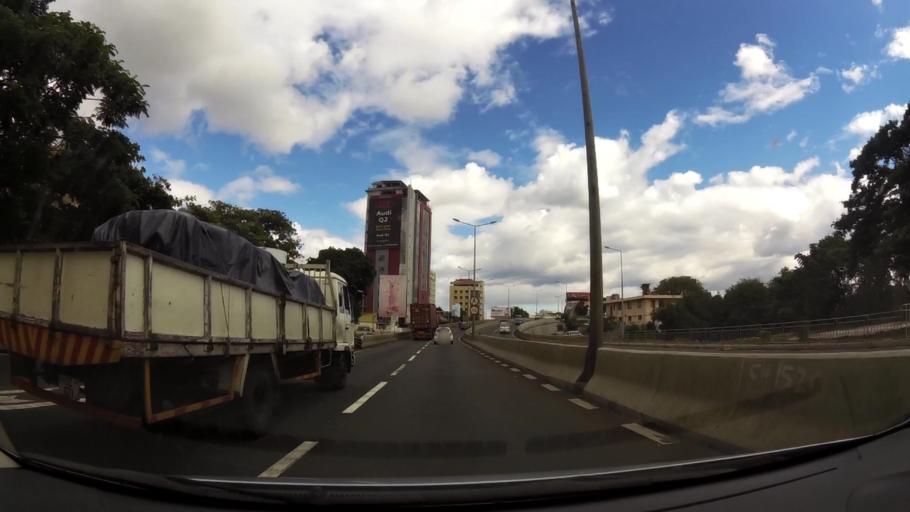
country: MU
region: Port Louis
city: Port Louis
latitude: -20.1639
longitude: 57.4945
